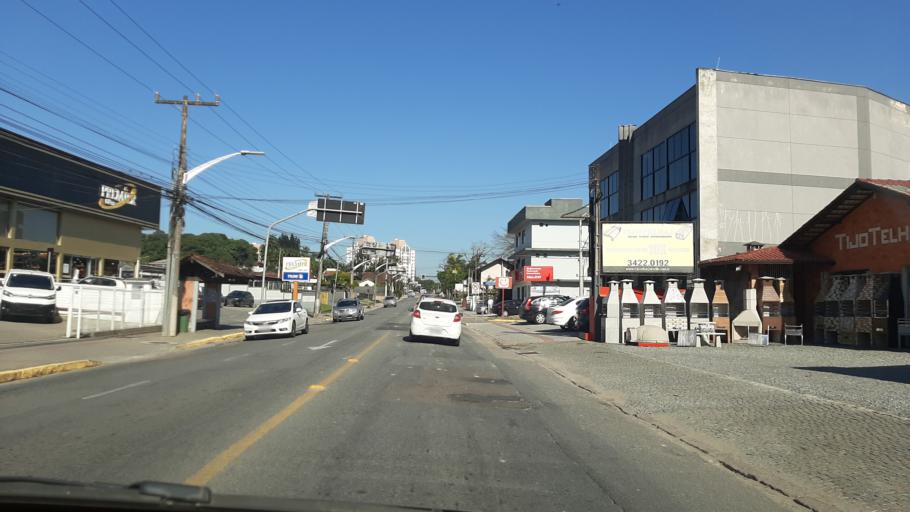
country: BR
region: Santa Catarina
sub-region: Joinville
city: Joinville
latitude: -26.3148
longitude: -48.8617
